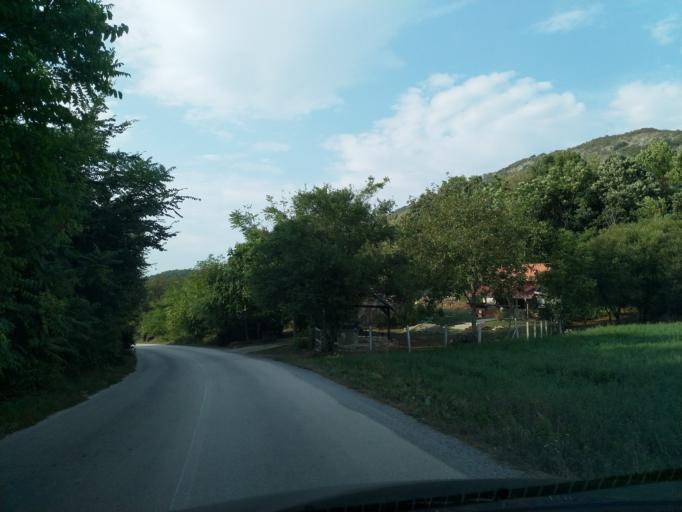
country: RS
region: Central Serbia
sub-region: Pomoravski Okrug
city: Paracin
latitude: 43.8365
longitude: 21.5402
